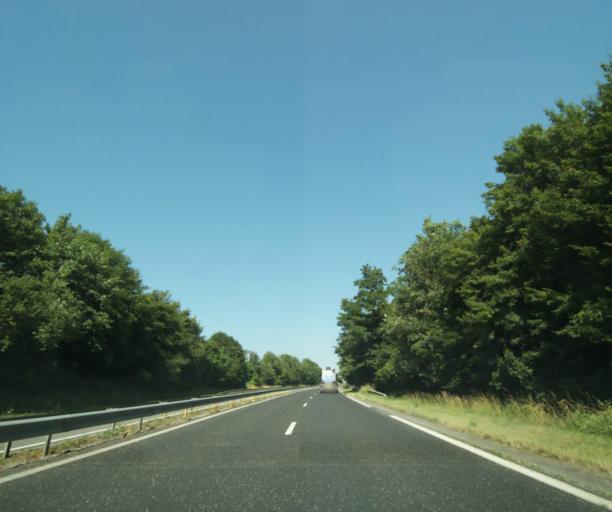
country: FR
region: Lorraine
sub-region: Departement de la Meuse
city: Longeville-en-Barrois
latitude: 48.6450
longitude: 5.1832
